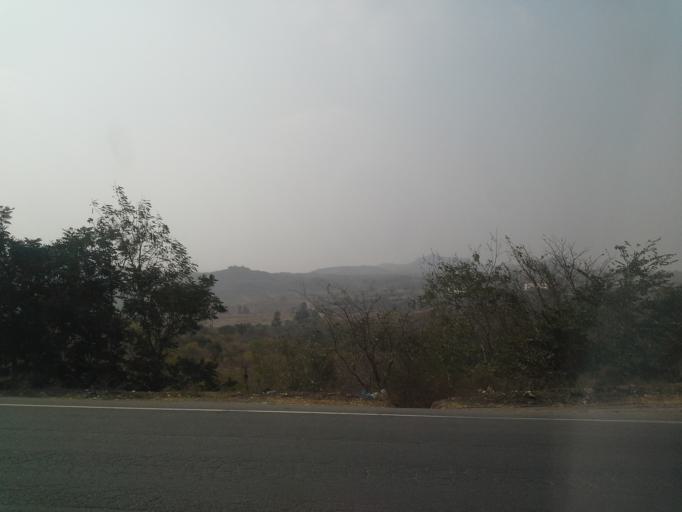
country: IN
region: Telangana
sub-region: Rangareddi
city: Lal Bahadur Nagar
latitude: 17.3167
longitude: 78.6679
